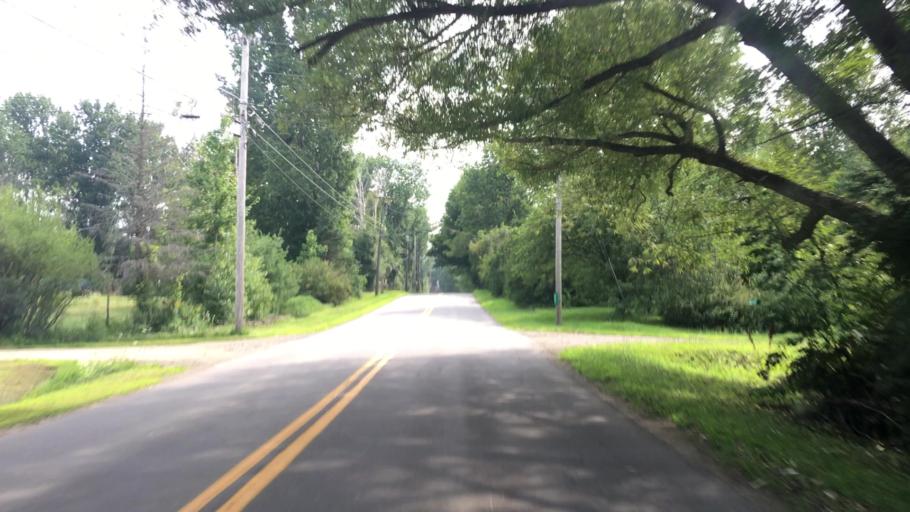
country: US
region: Maine
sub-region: Lincoln County
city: Jefferson
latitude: 44.1783
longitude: -69.4624
